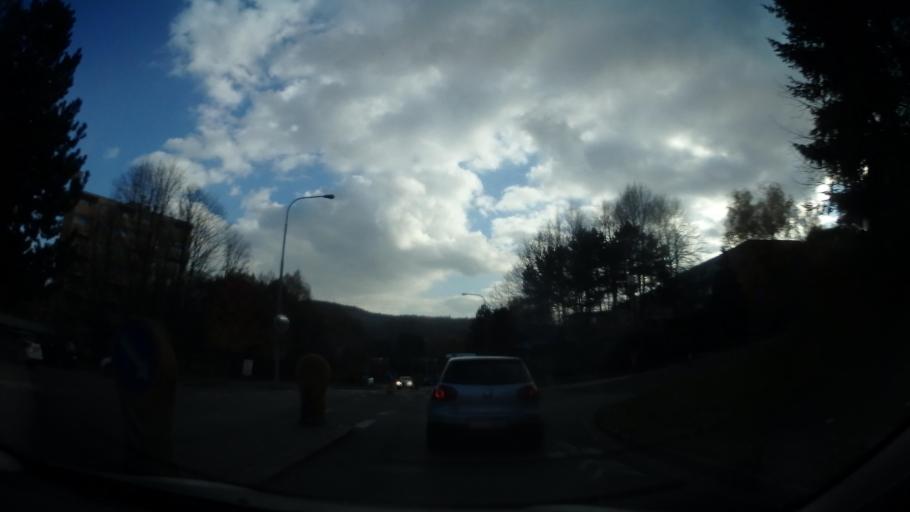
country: CZ
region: South Moravian
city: Troubsko
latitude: 49.2215
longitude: 16.5240
